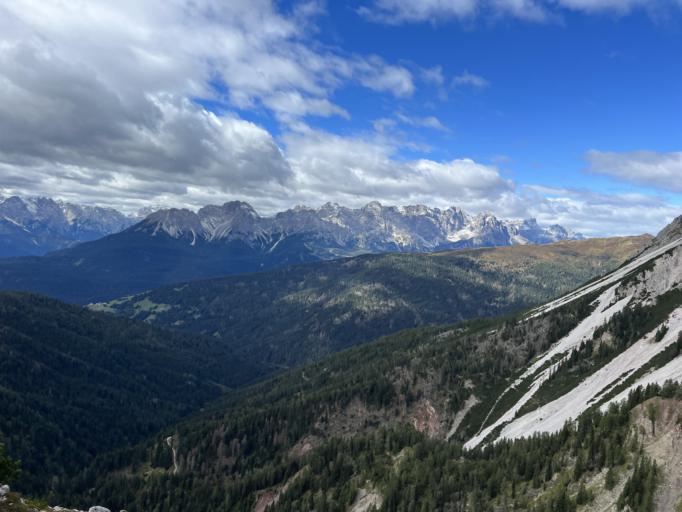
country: IT
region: Veneto
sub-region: Provincia di Belluno
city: San Pietro di Cadore
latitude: 46.6160
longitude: 12.5753
